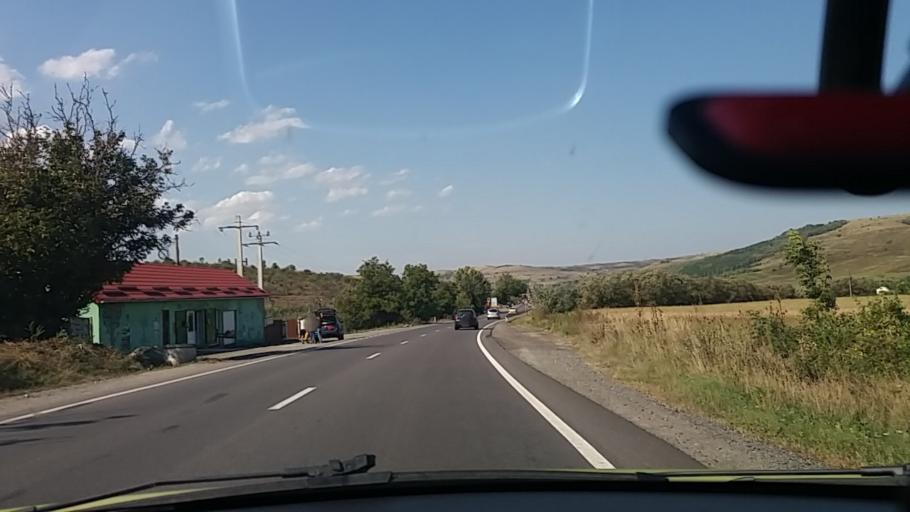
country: RO
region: Sibiu
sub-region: Comuna Slimnic
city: Slimnic
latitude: 45.8961
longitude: 24.1620
